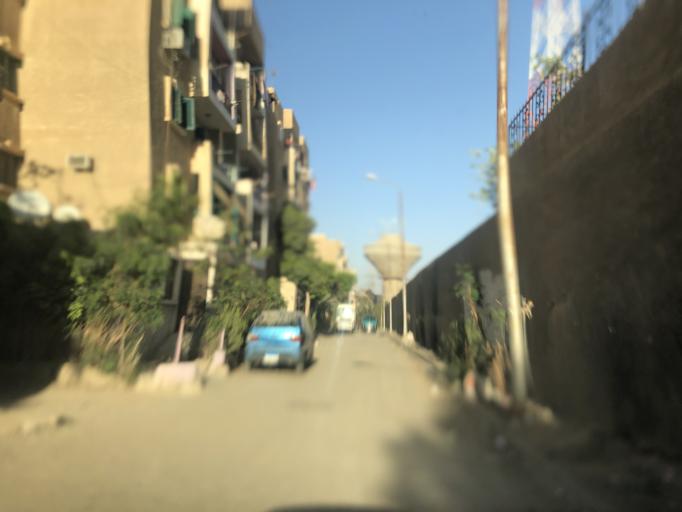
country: EG
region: Al Jizah
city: Al Jizah
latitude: 29.9881
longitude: 31.1056
